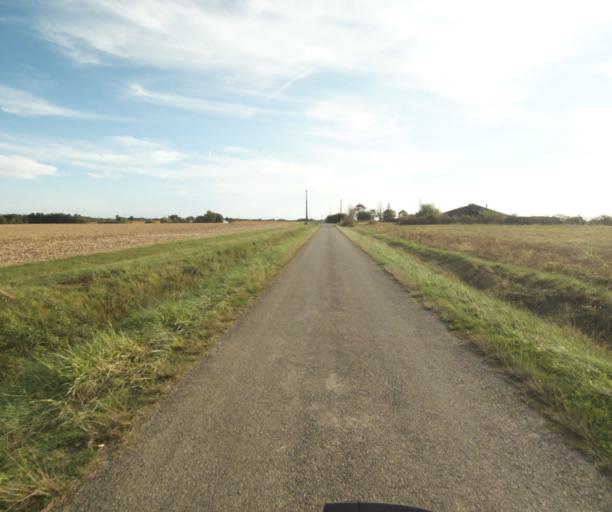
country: FR
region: Midi-Pyrenees
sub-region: Departement du Tarn-et-Garonne
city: Finhan
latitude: 43.9146
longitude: 1.1314
